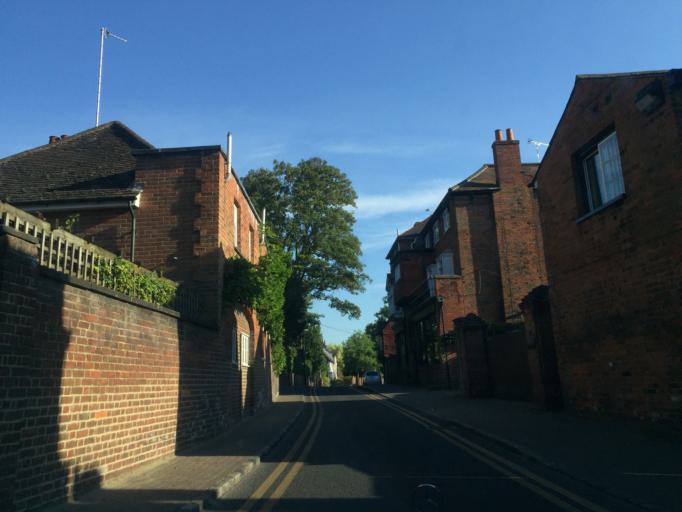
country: GB
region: England
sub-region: Wokingham
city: Wargrave
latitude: 51.5005
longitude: -0.8701
